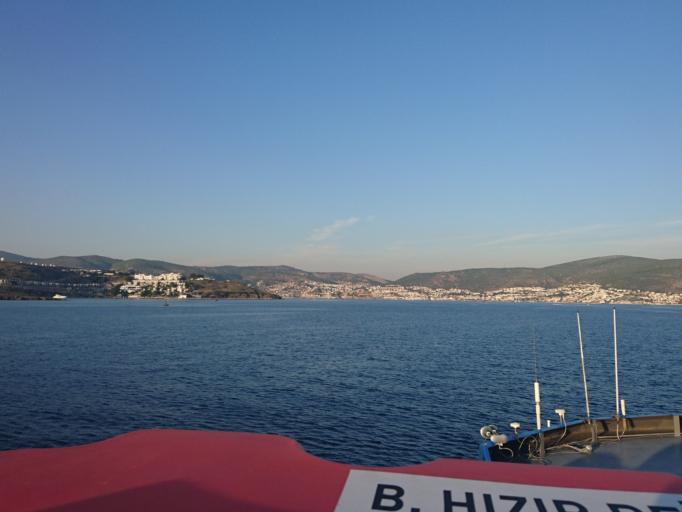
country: TR
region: Mugla
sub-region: Bodrum
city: Bodrum
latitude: 37.0108
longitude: 27.4128
